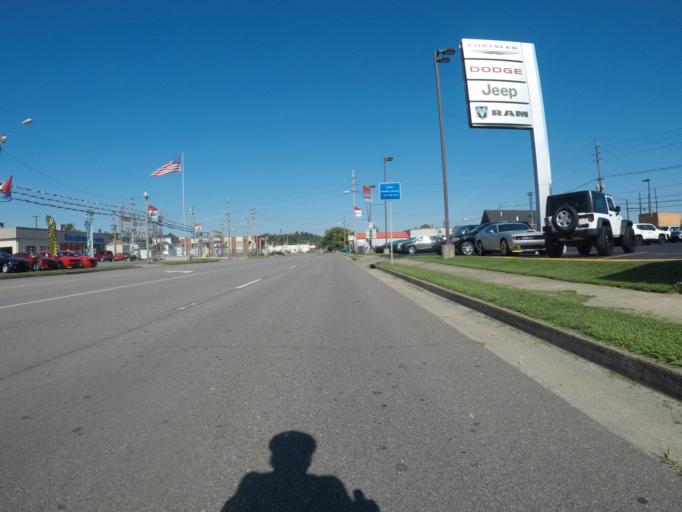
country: US
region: Kentucky
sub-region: Boyd County
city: Ashland
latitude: 38.4827
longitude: -82.6447
